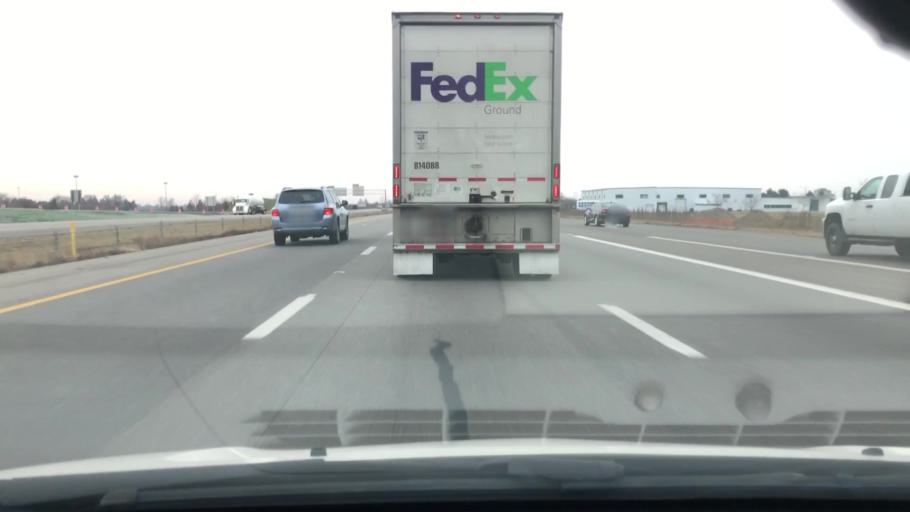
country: US
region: Ohio
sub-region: Wood County
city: Bowling Green
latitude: 41.3748
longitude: -83.6160
